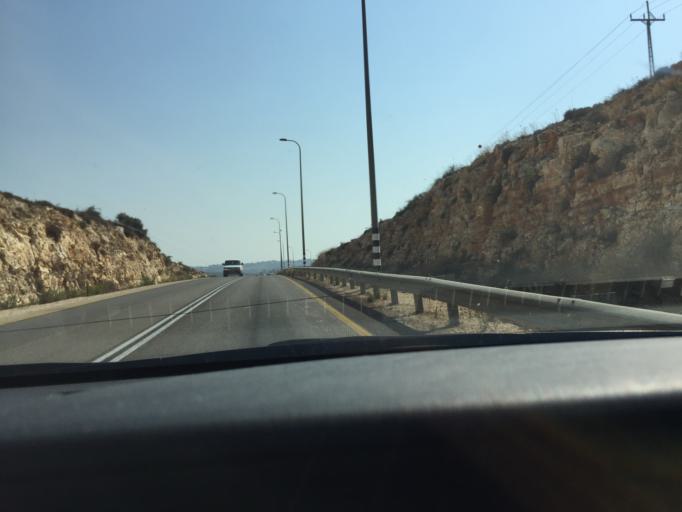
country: PS
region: West Bank
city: Bruqin
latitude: 32.0842
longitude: 35.1036
